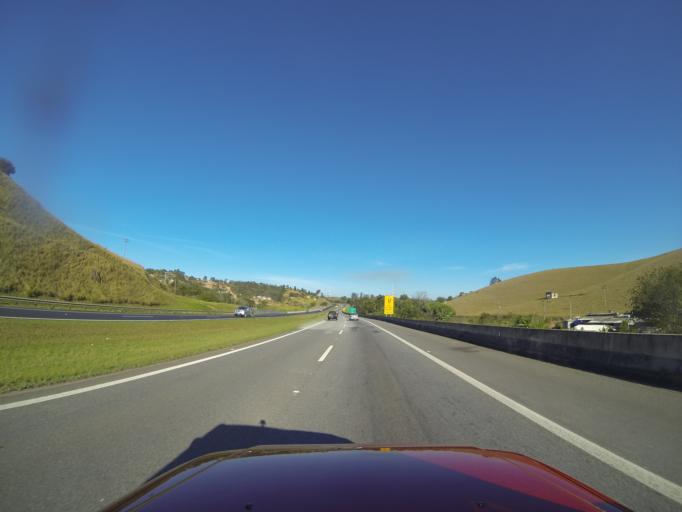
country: BR
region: Sao Paulo
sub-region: Santa Isabel
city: Santa Isabel
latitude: -23.1822
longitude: -46.2052
